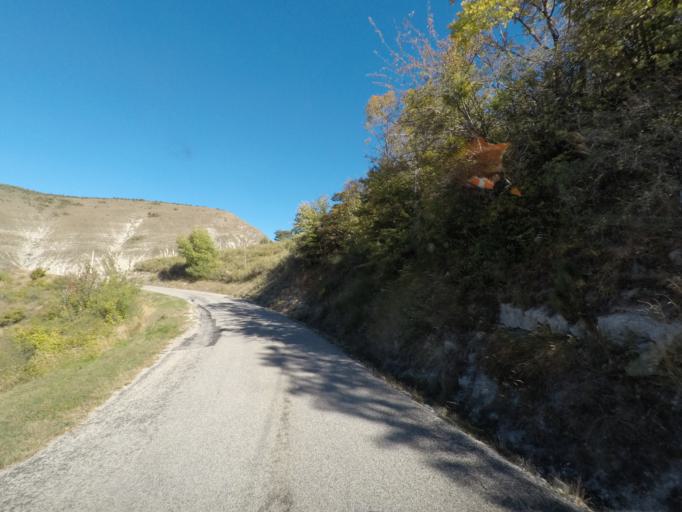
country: FR
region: Rhone-Alpes
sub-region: Departement de la Drome
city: Die
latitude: 44.5310
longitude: 5.3657
